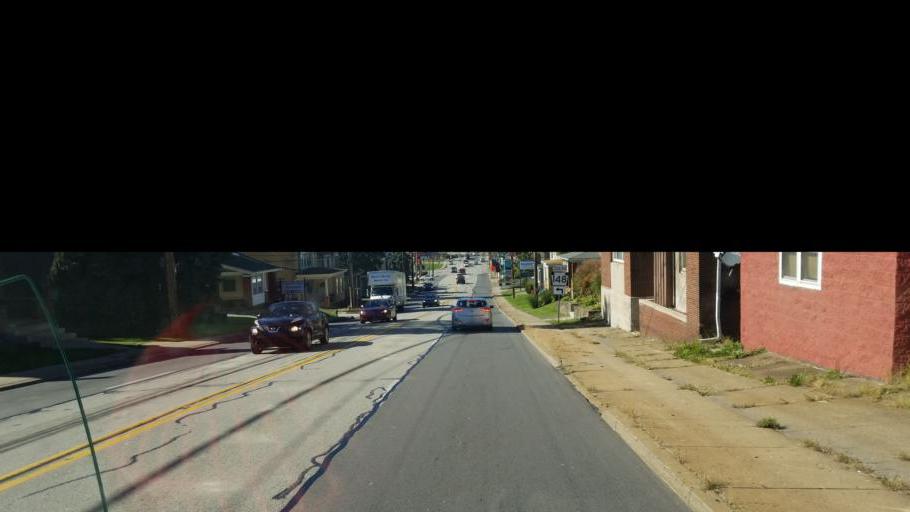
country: US
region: Pennsylvania
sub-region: Allegheny County
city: North Versailles
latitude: 40.3803
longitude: -79.8093
